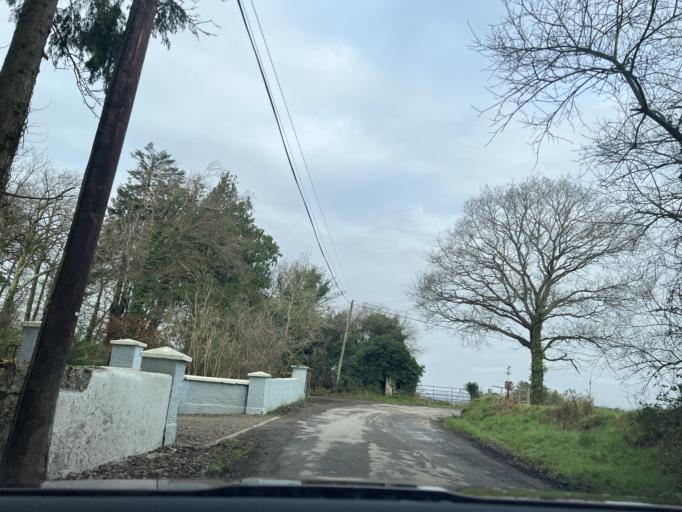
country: IE
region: Leinster
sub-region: Loch Garman
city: Castlebridge
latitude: 52.3786
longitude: -6.5467
